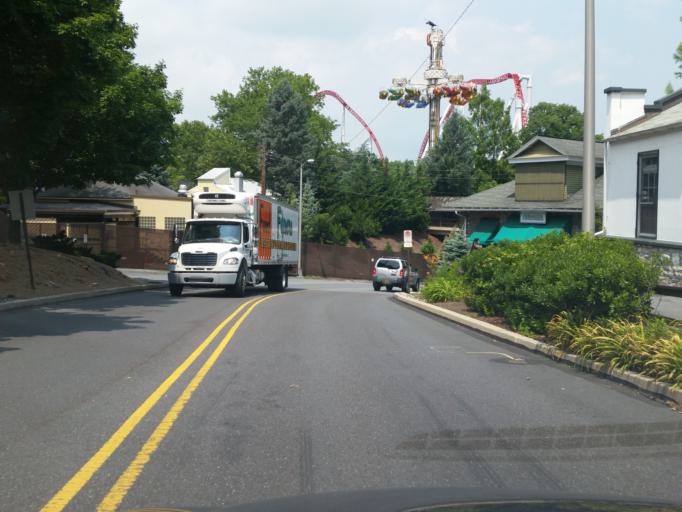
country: US
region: Pennsylvania
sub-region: Dauphin County
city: Hershey
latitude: 40.2876
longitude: -76.6521
